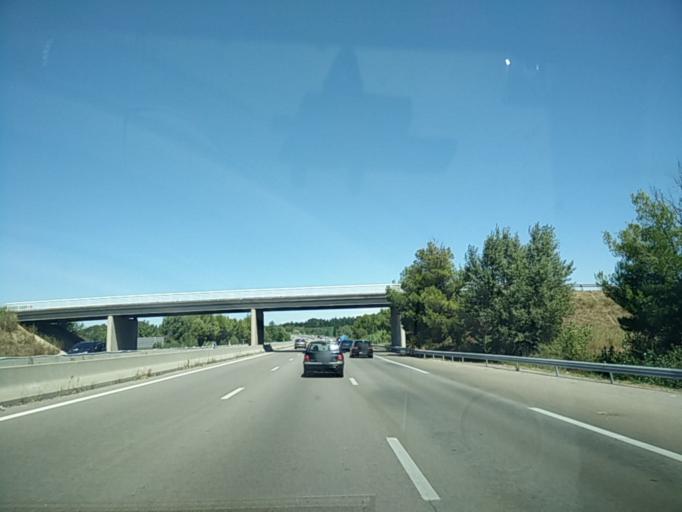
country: FR
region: Provence-Alpes-Cote d'Azur
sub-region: Departement du Vaucluse
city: Morieres-les-Avignon
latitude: 43.9098
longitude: 4.9135
